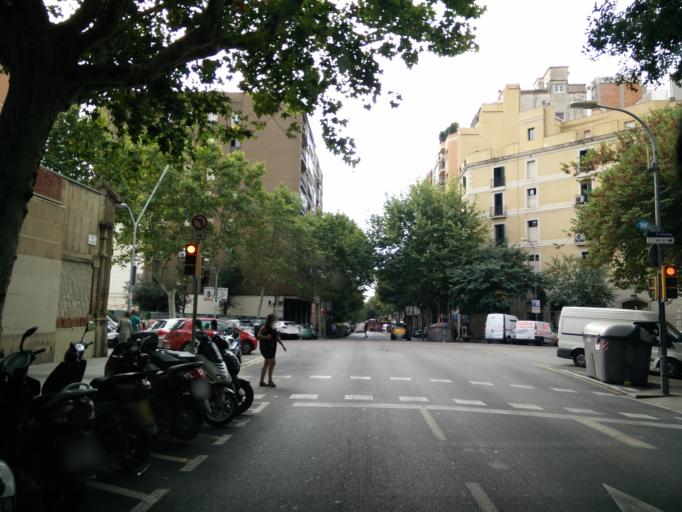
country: ES
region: Catalonia
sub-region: Provincia de Barcelona
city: Barcelona
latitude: 41.3884
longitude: 2.1525
